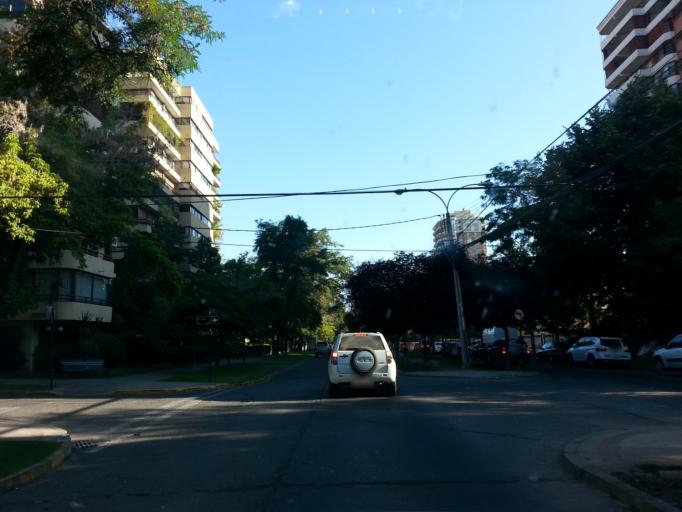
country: CL
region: Santiago Metropolitan
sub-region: Provincia de Santiago
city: Villa Presidente Frei, Nunoa, Santiago, Chile
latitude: -33.4278
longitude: -70.5980
